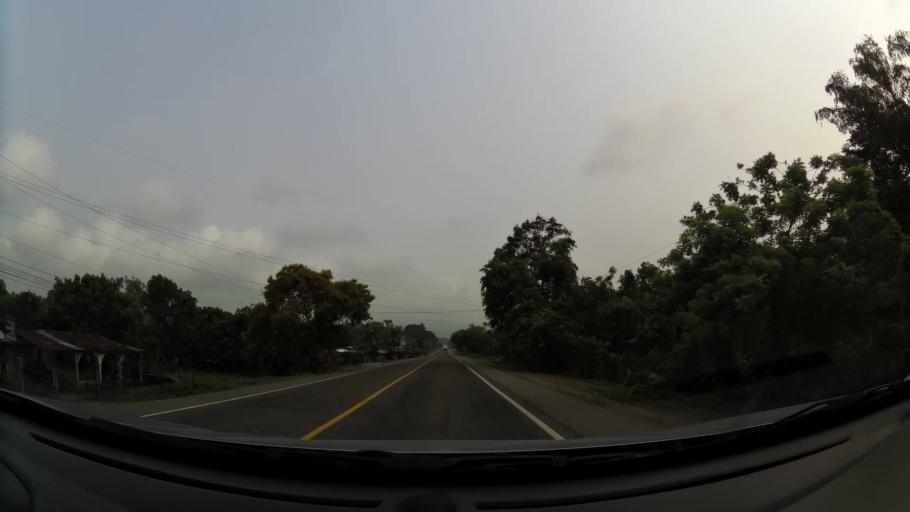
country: HN
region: Atlantida
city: Mezapa
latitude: 15.6098
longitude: -87.6131
